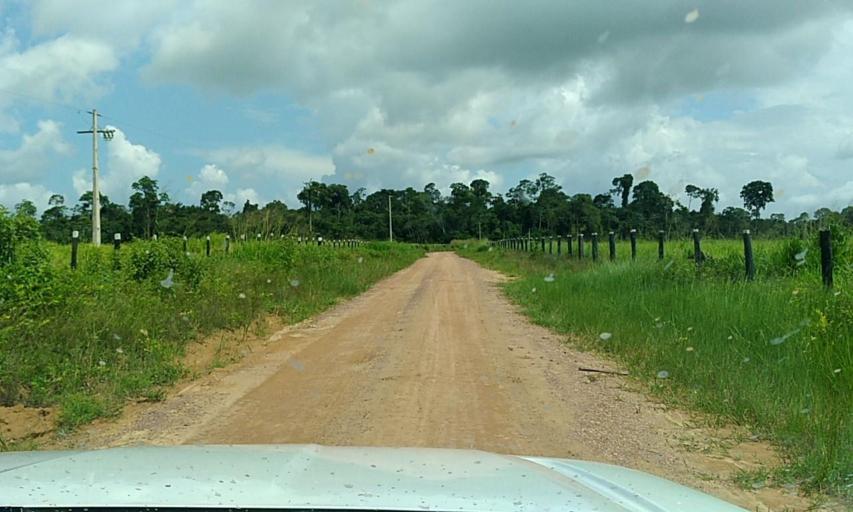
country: BR
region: Para
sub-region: Senador Jose Porfirio
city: Senador Jose Porfirio
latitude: -2.5140
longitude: -51.8413
